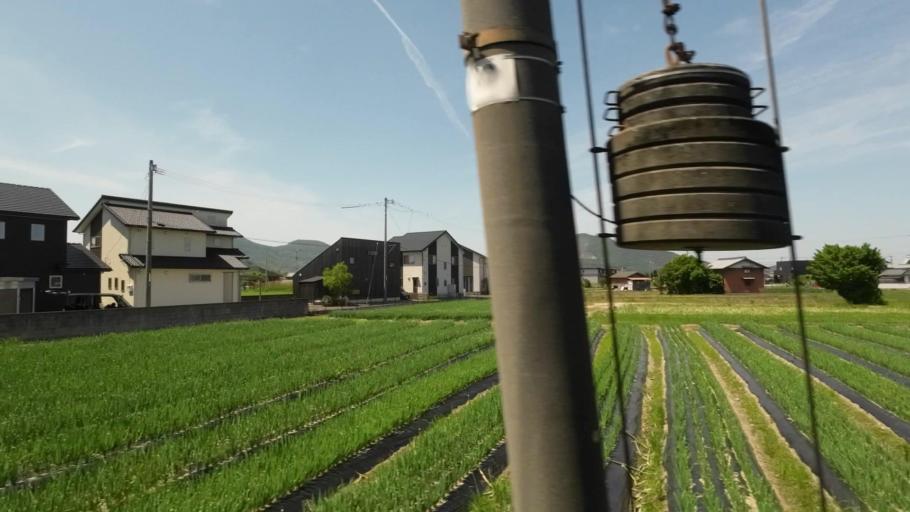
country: JP
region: Kagawa
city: Marugame
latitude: 34.2469
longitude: 133.7784
